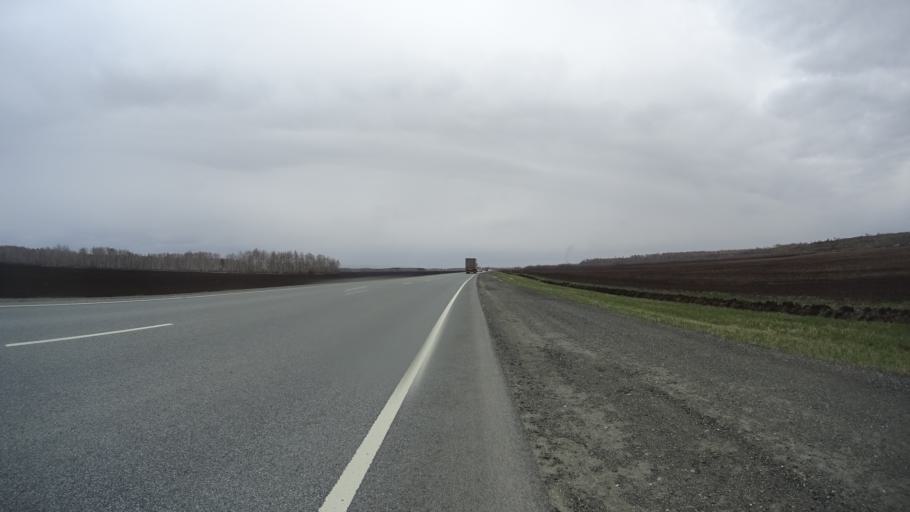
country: RU
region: Chelyabinsk
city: Krasnogorskiy
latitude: 54.5776
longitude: 61.2915
